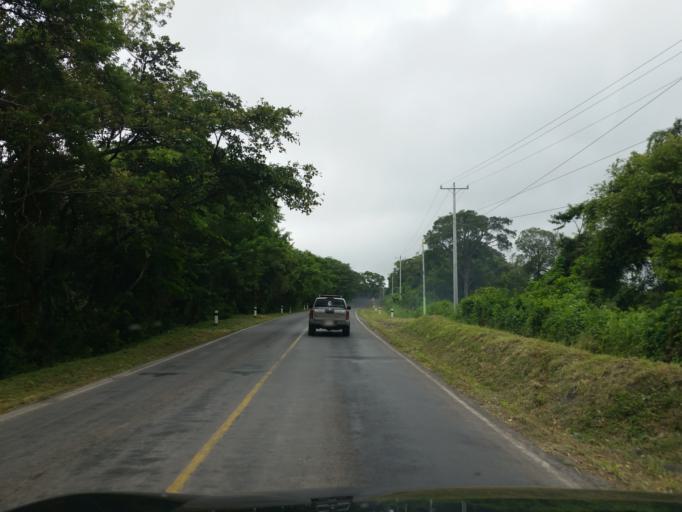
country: NI
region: Managua
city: El Crucero
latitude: 12.0233
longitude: -86.3126
